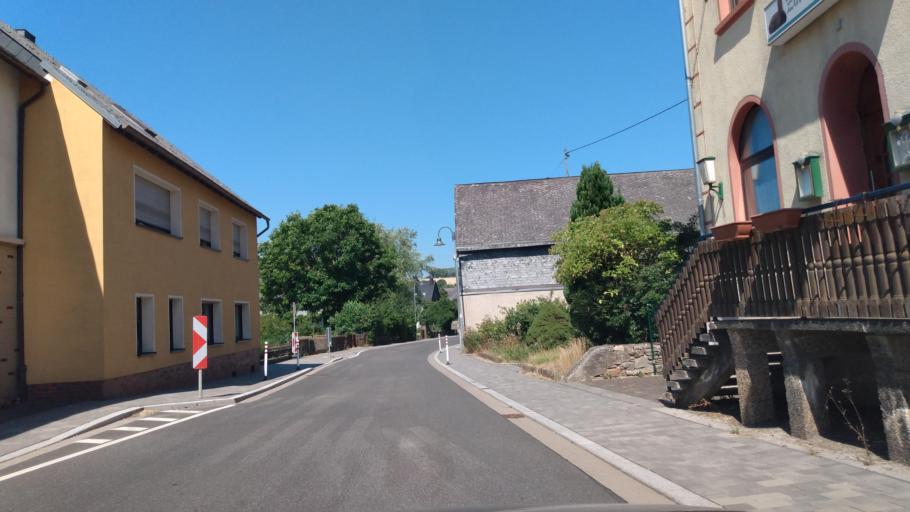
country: DE
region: Rheinland-Pfalz
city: Hochscheid
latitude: 49.8471
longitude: 7.1802
